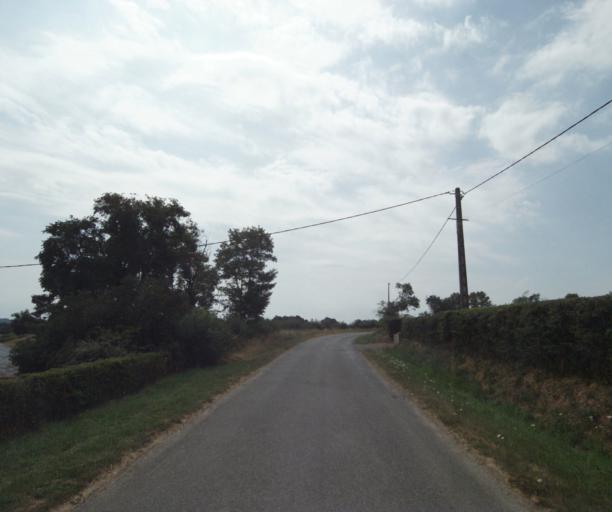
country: FR
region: Bourgogne
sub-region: Departement de Saone-et-Loire
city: Gueugnon
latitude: 46.5895
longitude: 4.0397
